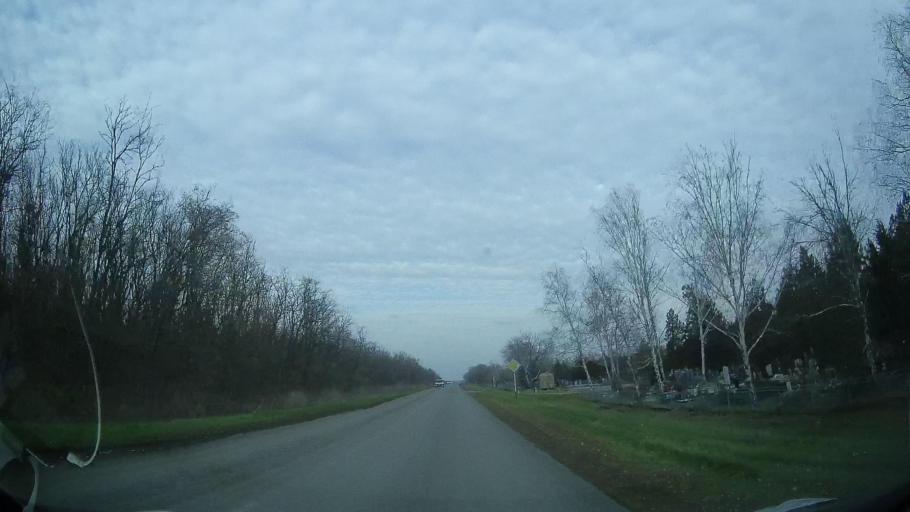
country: RU
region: Rostov
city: Zernograd
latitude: 46.8741
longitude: 40.3335
